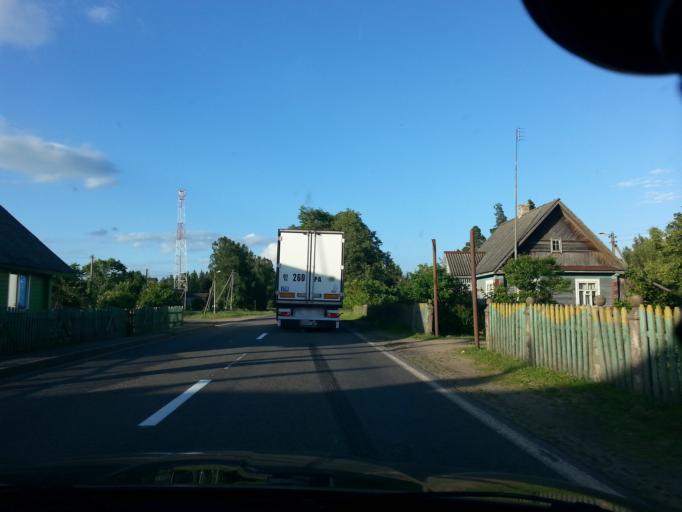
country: BY
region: Minsk
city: Svir
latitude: 54.9195
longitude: 26.4606
